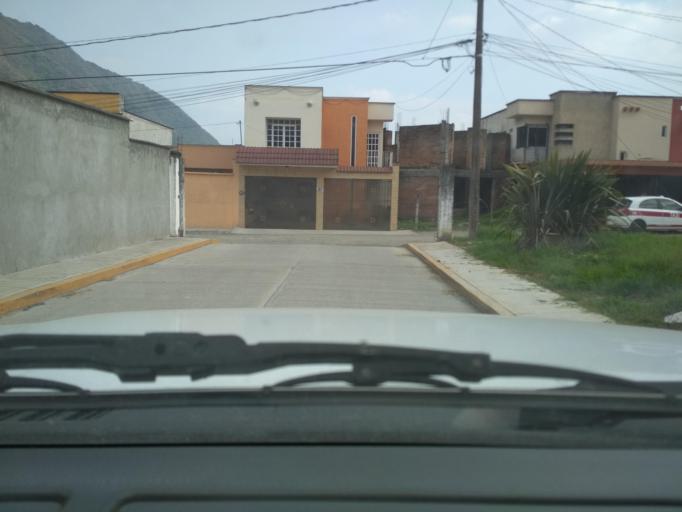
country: MX
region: Veracruz
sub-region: Mariano Escobedo
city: Palmira
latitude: 18.8736
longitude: -97.1015
